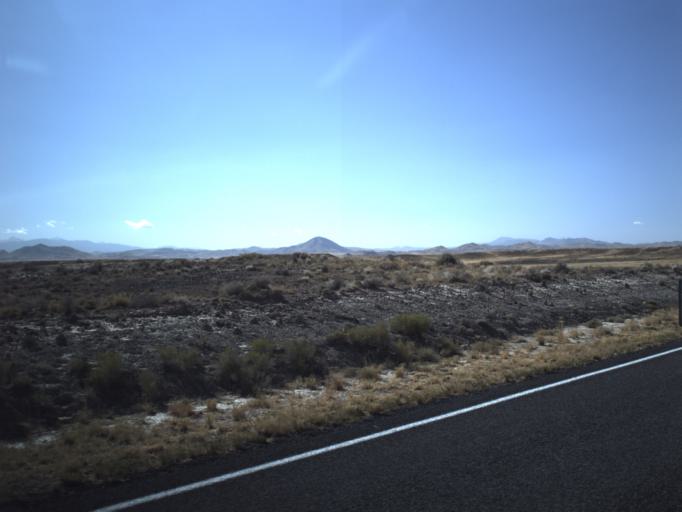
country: US
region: Utah
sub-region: Millard County
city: Fillmore
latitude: 38.8926
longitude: -112.8264
